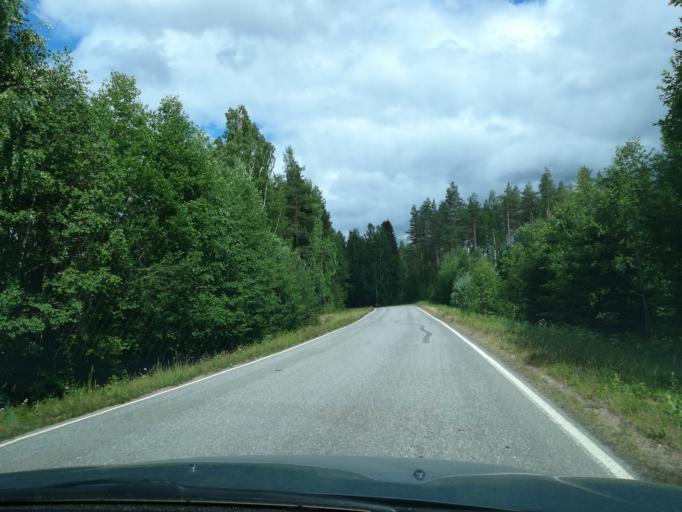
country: FI
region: South Karelia
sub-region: Lappeenranta
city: Savitaipale
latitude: 61.2534
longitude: 27.7090
